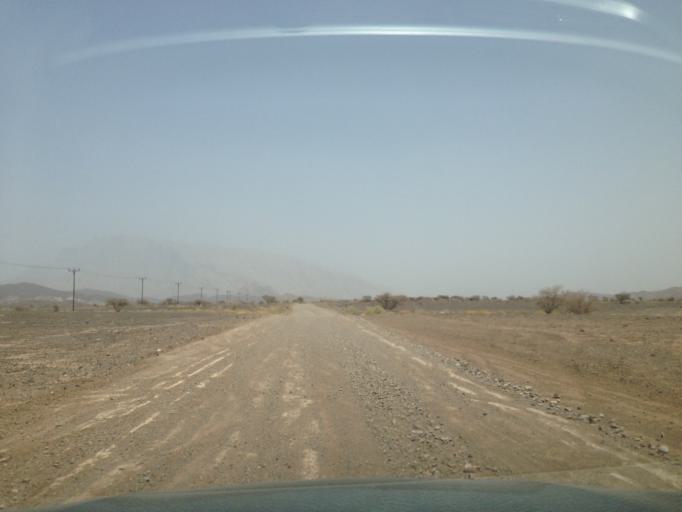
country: OM
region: Az Zahirah
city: `Ibri
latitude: 23.2231
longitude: 56.8226
